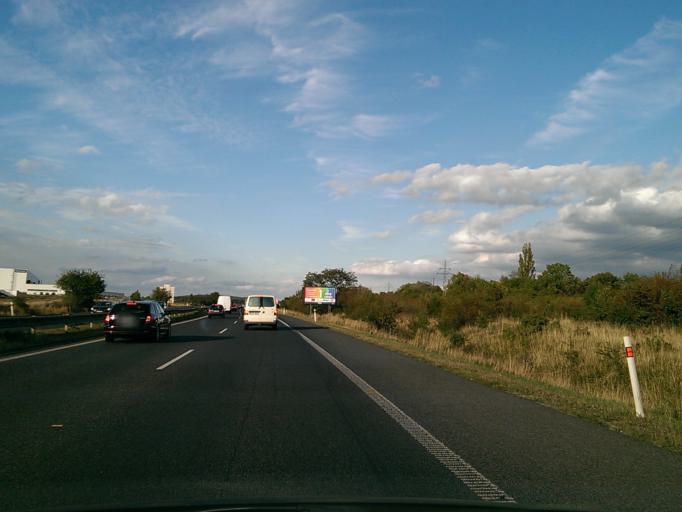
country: CZ
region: Central Bohemia
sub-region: Okres Mlada Boleslav
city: Mlada Boleslav
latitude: 50.3891
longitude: 14.9050
